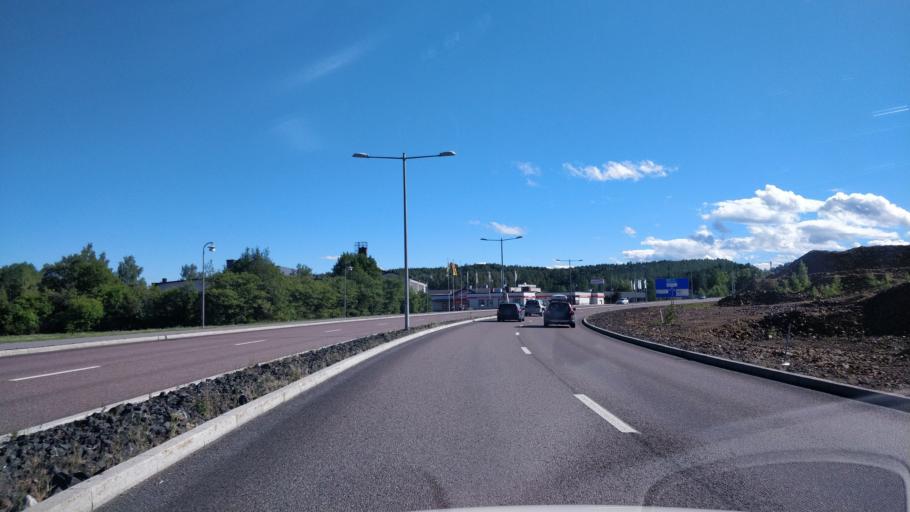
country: SE
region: Dalarna
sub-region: Faluns Kommun
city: Falun
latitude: 60.5997
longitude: 15.6221
